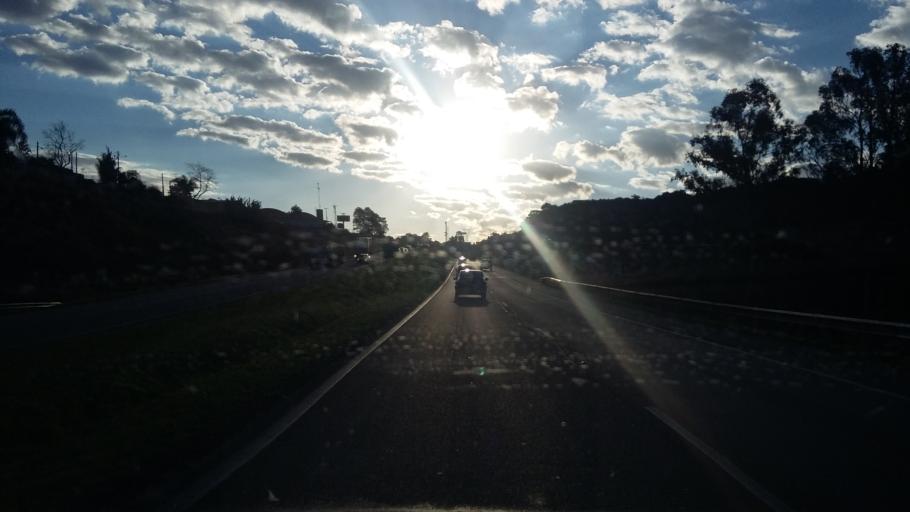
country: BR
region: Parana
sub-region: Campo Largo
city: Campo Largo
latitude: -25.4337
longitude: -49.4162
